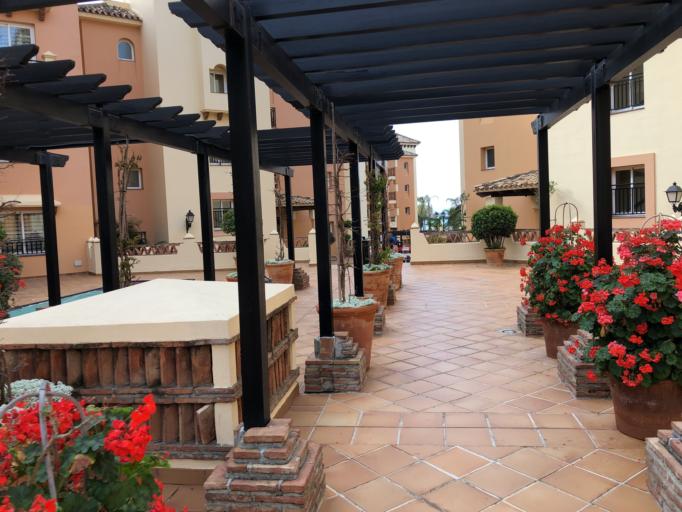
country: ES
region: Andalusia
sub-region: Provincia de Malaga
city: Ojen
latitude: 36.4903
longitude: -4.7707
